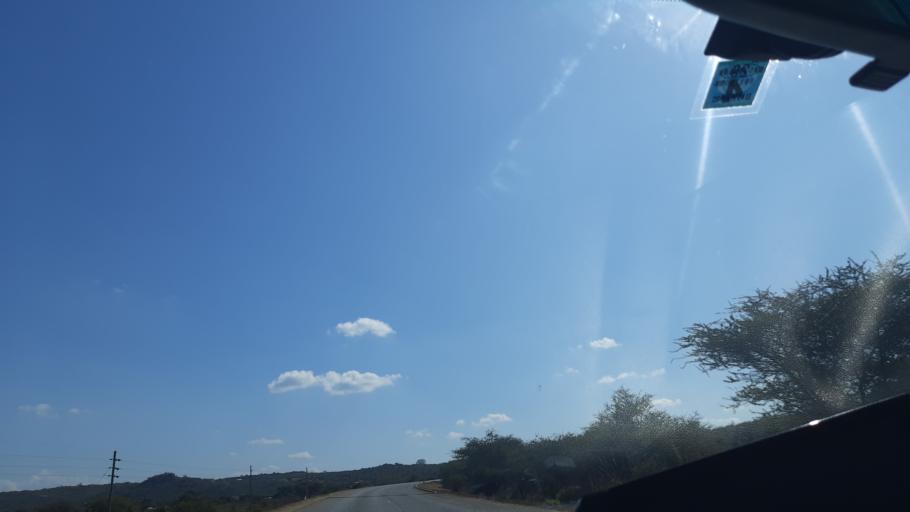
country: TZ
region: Singida
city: Kilimatinde
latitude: -5.7825
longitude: 34.8896
